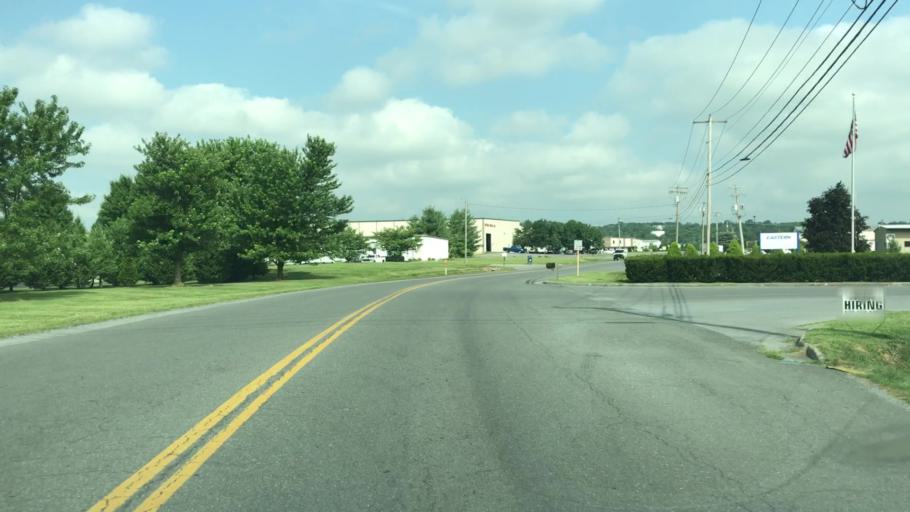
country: US
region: Virginia
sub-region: City of Winchester
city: Winchester
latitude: 39.2211
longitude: -78.1458
